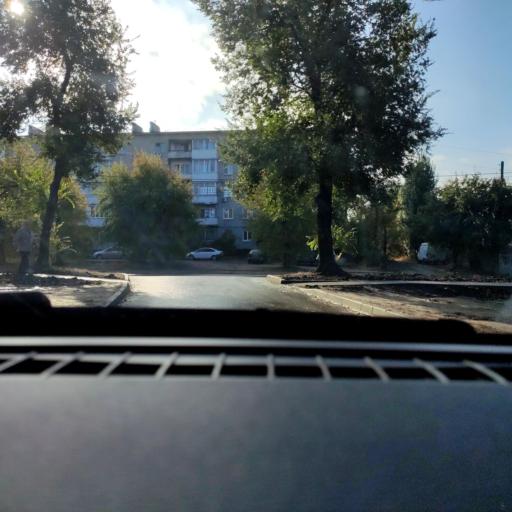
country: RU
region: Voronezj
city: Maslovka
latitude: 51.6161
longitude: 39.2412
